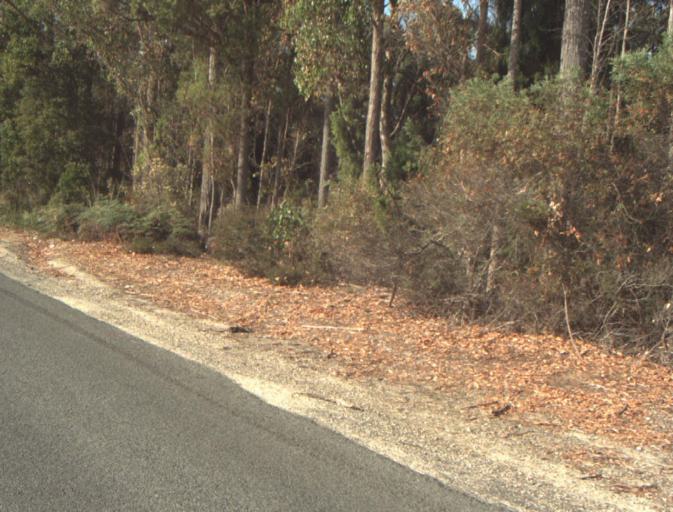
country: AU
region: Tasmania
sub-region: Dorset
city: Bridport
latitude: -41.1675
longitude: 147.2620
